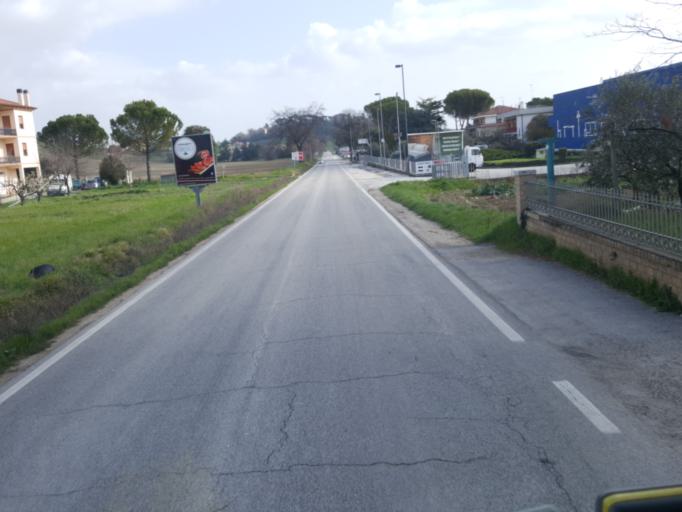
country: IT
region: The Marches
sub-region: Provincia di Macerata
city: Passo di Treia
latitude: 43.2910
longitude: 13.3386
